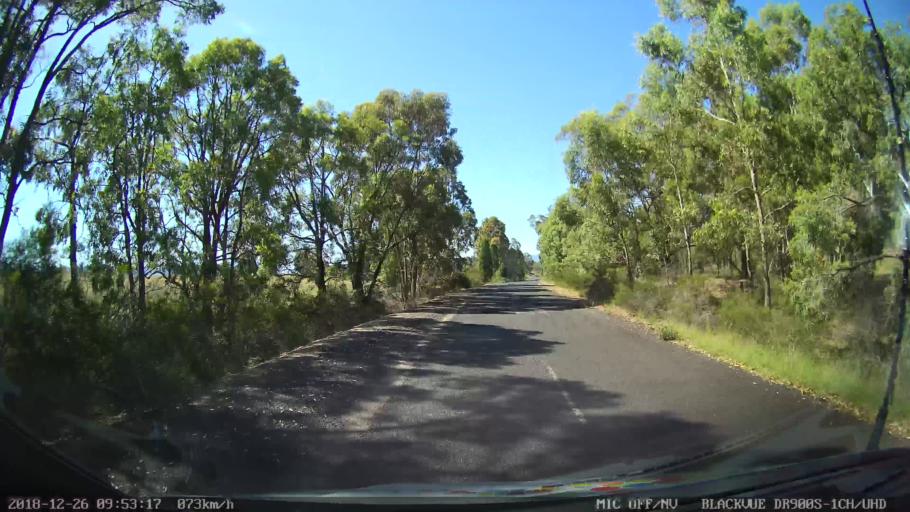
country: AU
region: New South Wales
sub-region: Mid-Western Regional
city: Kandos
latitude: -33.0191
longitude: 150.1531
